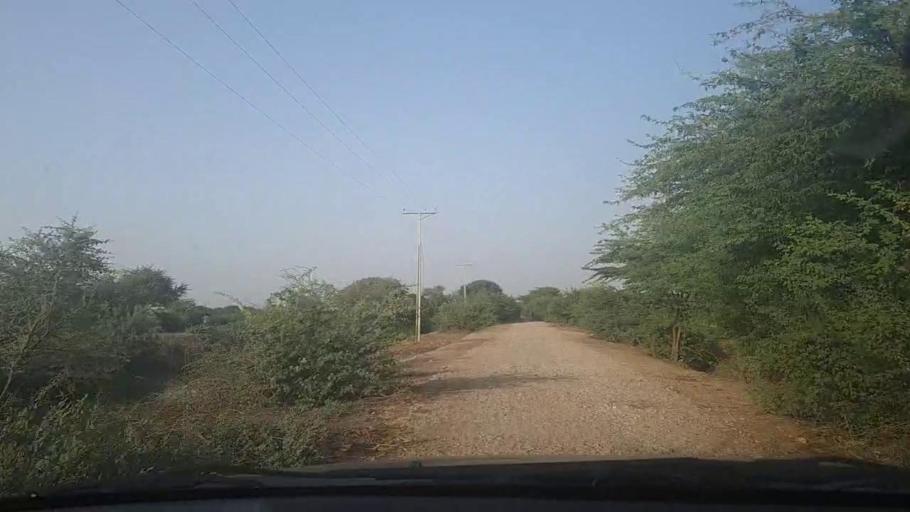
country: PK
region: Sindh
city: Keti Bandar
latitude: 24.2819
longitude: 67.5996
